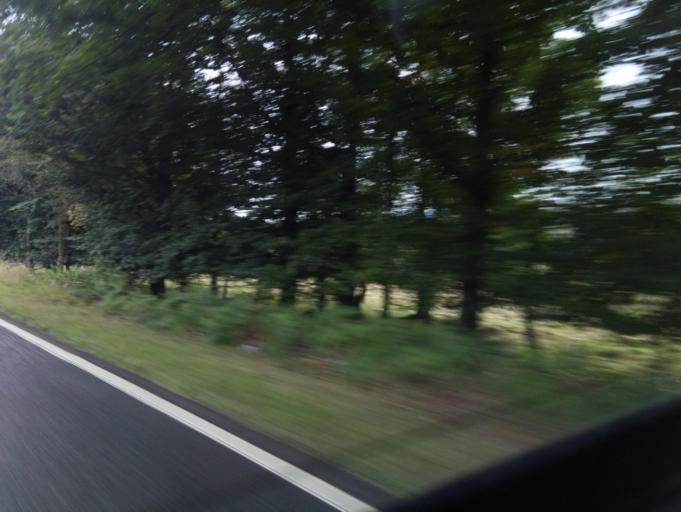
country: GB
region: Scotland
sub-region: Dumfries and Galloway
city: Moffat
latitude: 55.2465
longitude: -3.4610
